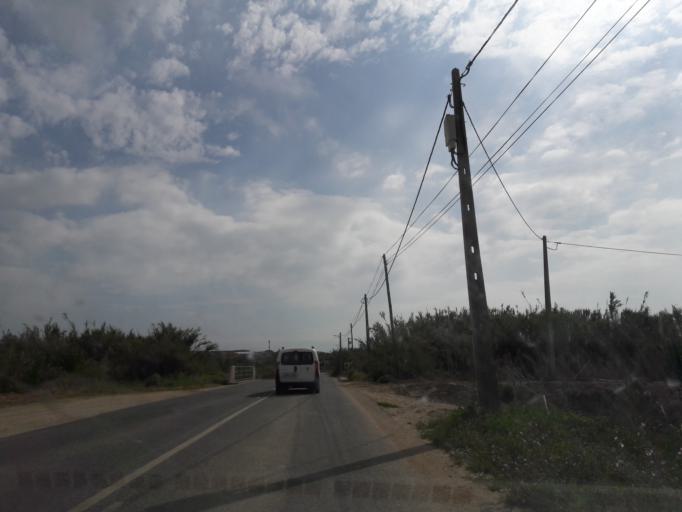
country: PT
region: Leiria
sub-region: Peniche
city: Atouguia da Baleia
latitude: 39.3463
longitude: -9.3254
